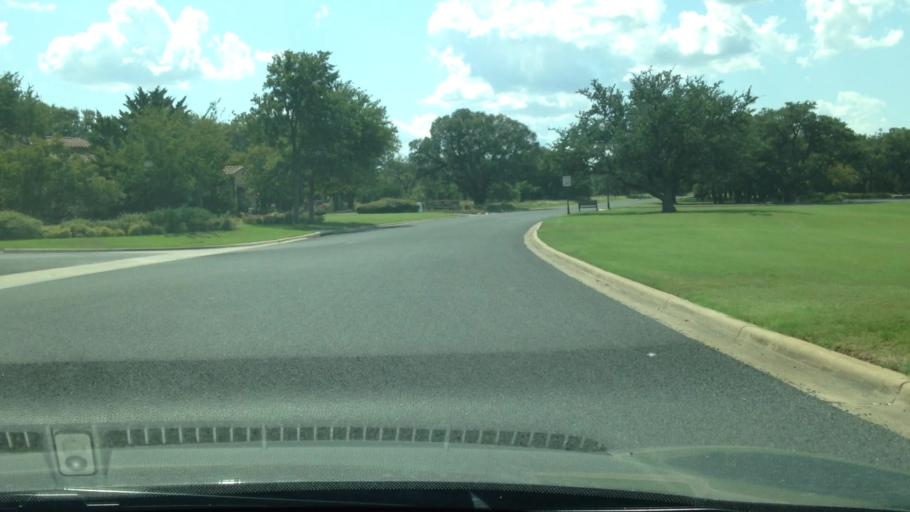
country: US
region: Texas
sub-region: Williamson County
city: Leander
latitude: 30.6378
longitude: -97.7925
